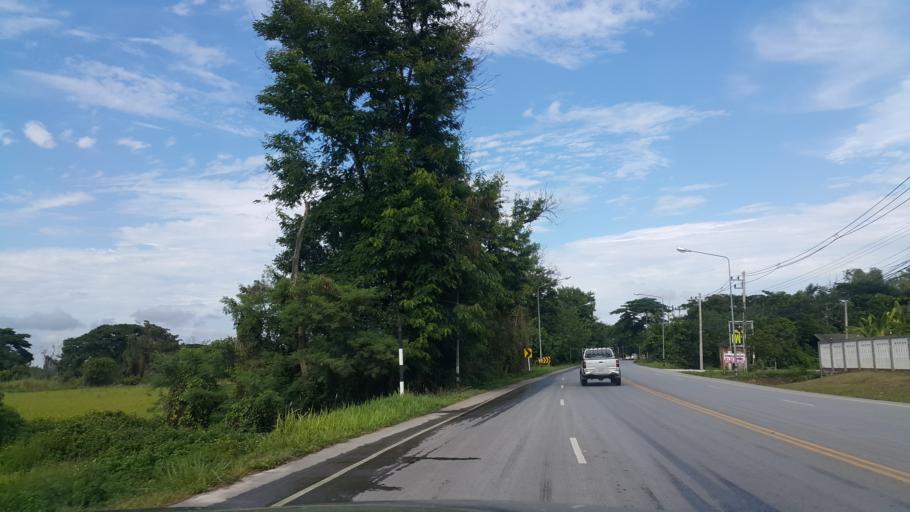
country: TH
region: Chiang Rai
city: Chiang Rai
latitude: 19.9131
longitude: 99.8675
